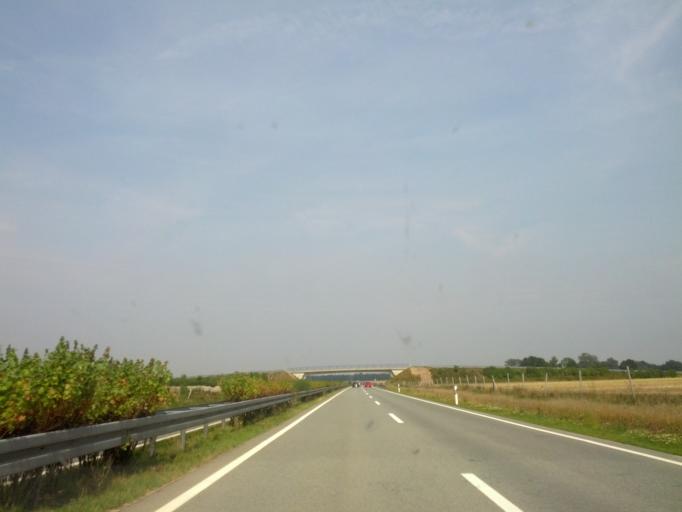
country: DE
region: Mecklenburg-Vorpommern
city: Wittenhagen
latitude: 54.1102
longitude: 13.1480
